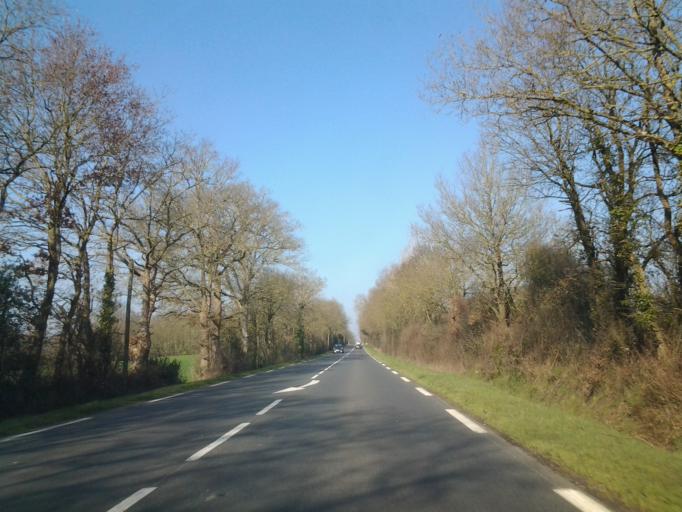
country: FR
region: Pays de la Loire
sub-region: Departement de la Vendee
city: Mache
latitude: 46.7811
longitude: -1.6878
